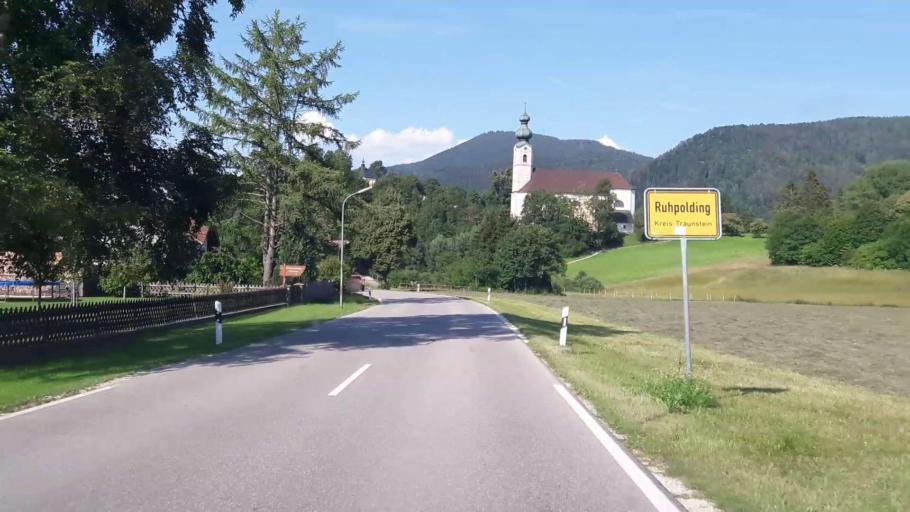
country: DE
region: Bavaria
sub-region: Upper Bavaria
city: Ruhpolding
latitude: 47.7604
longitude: 12.6381
